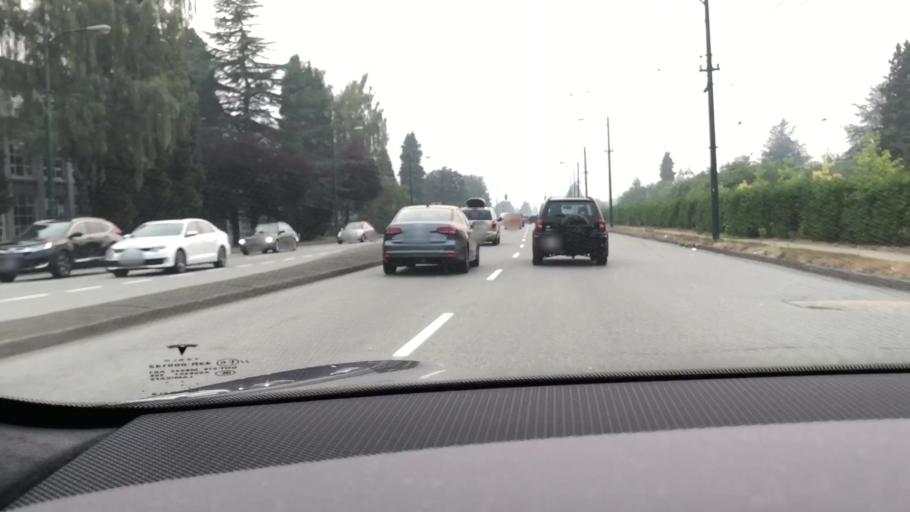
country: CA
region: British Columbia
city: Vancouver
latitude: 49.2330
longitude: -123.0919
